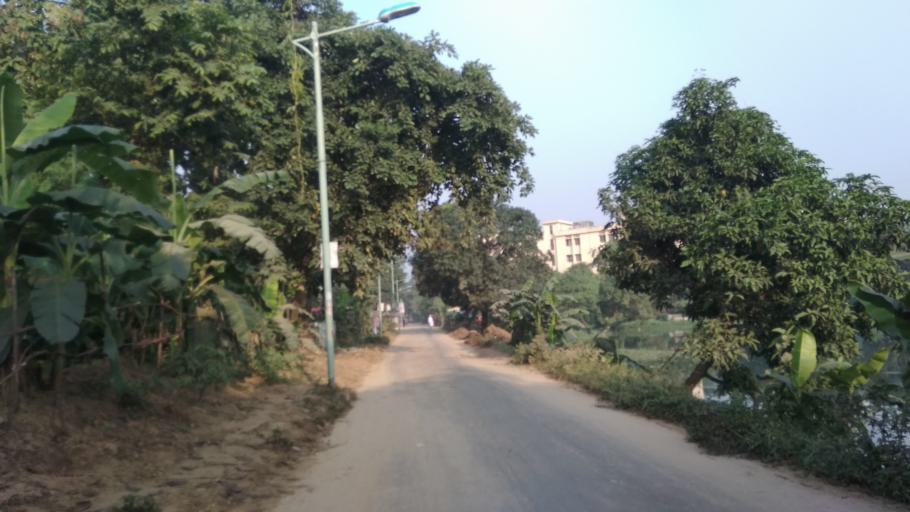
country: BD
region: Dhaka
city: Tungi
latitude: 23.8431
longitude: 90.4185
